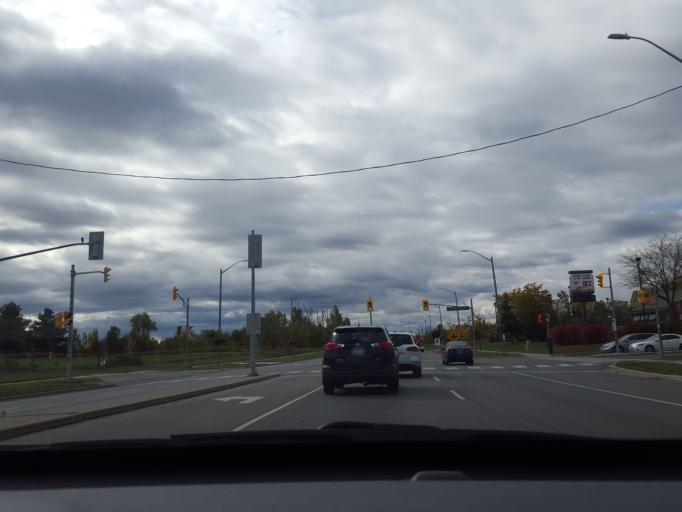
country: CA
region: Ontario
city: Markham
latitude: 43.8329
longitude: -79.3053
